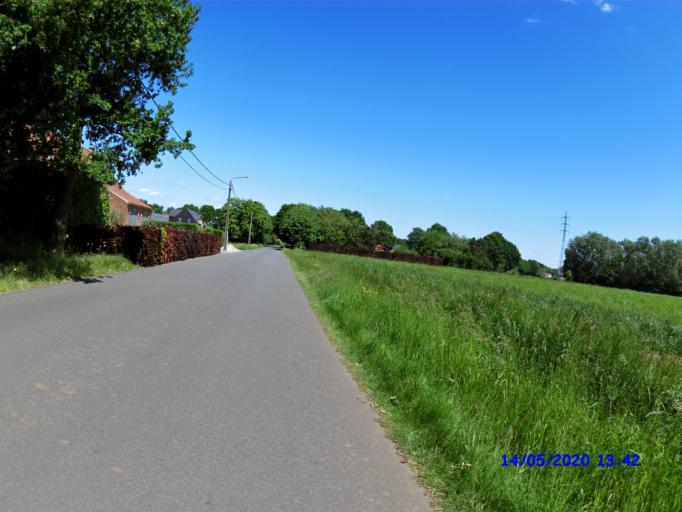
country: BE
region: Flanders
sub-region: Provincie Antwerpen
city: Geel
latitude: 51.1744
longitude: 5.0054
